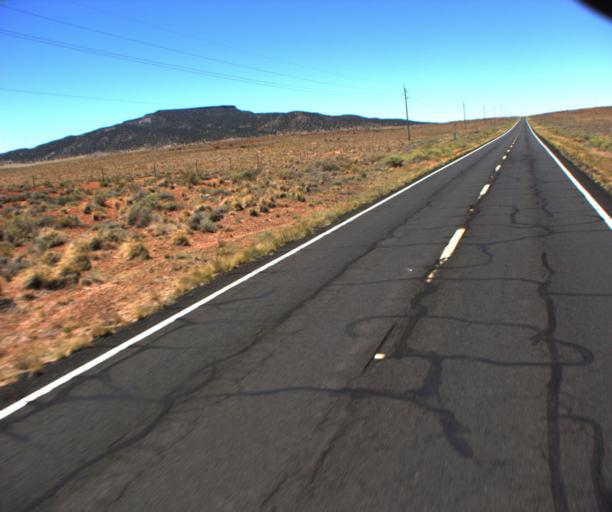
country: US
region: Arizona
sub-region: Coconino County
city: LeChee
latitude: 34.8880
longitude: -110.8731
